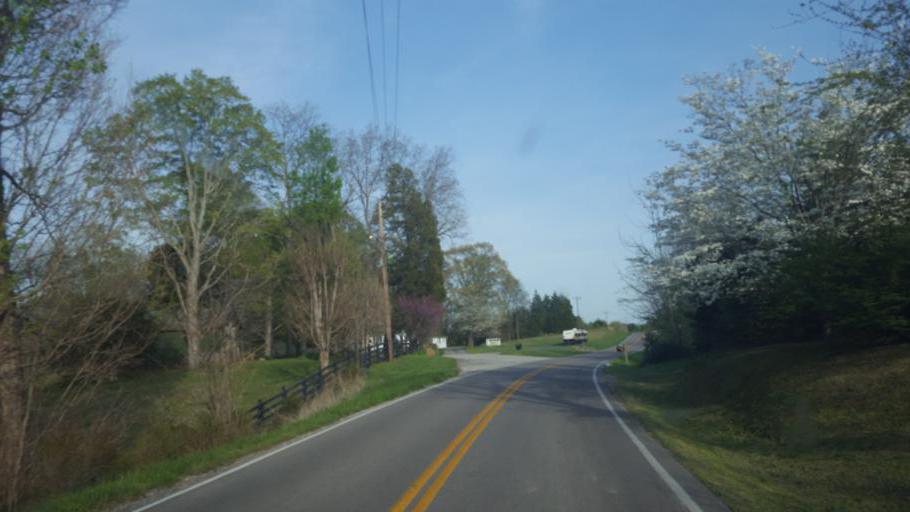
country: US
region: Kentucky
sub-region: Warren County
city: Plano
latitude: 36.9355
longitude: -86.3049
